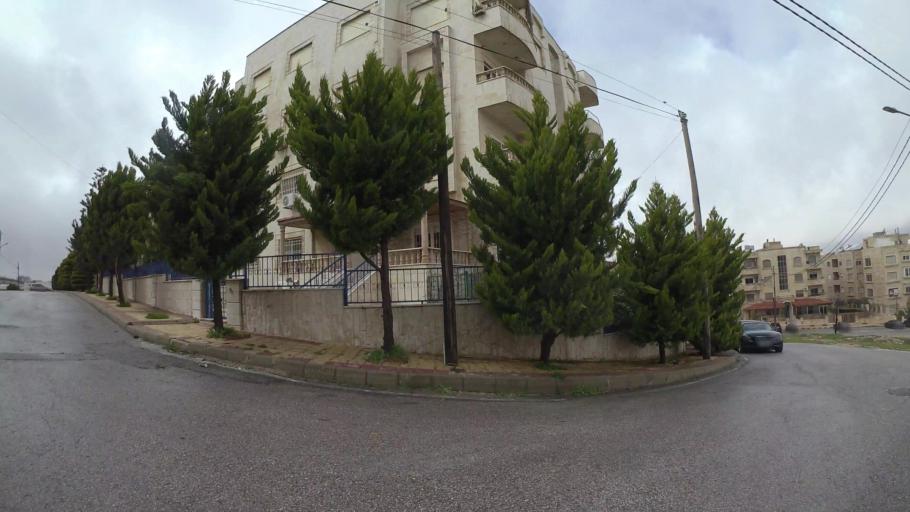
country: JO
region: Amman
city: Wadi as Sir
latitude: 31.9413
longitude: 35.8549
